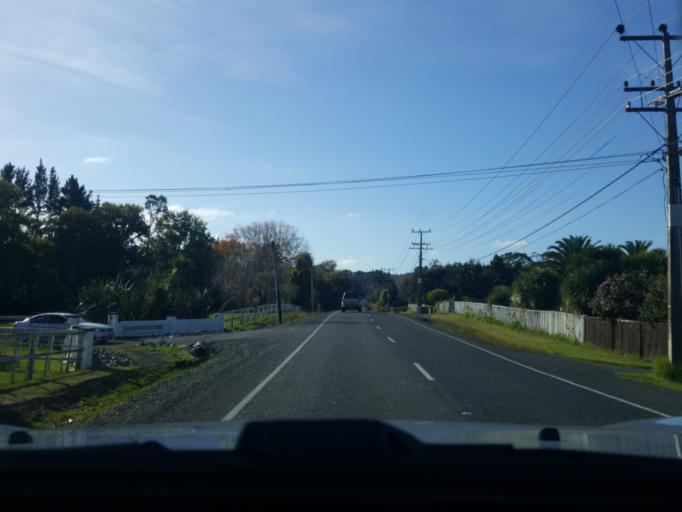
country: NZ
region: Auckland
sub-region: Auckland
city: Muriwai Beach
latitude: -36.7666
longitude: 174.5764
